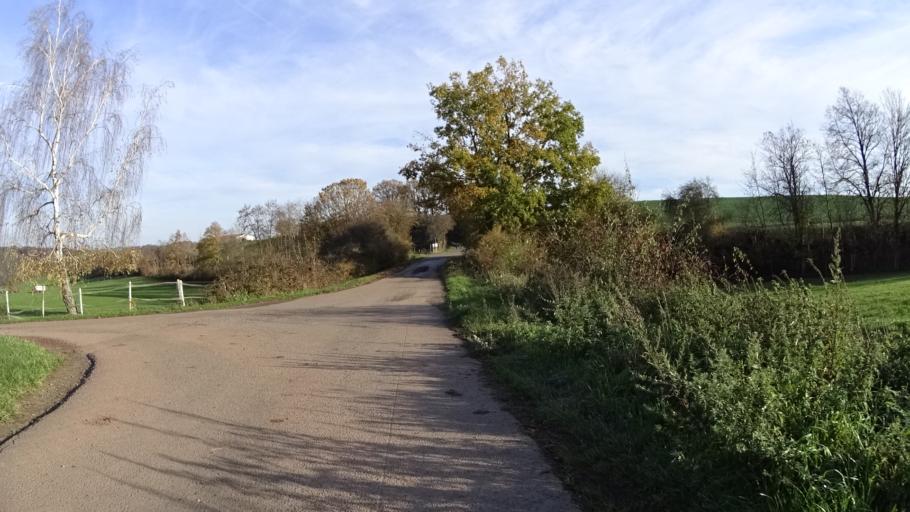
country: DE
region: Rheinland-Pfalz
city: Sien
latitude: 49.6948
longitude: 7.4926
